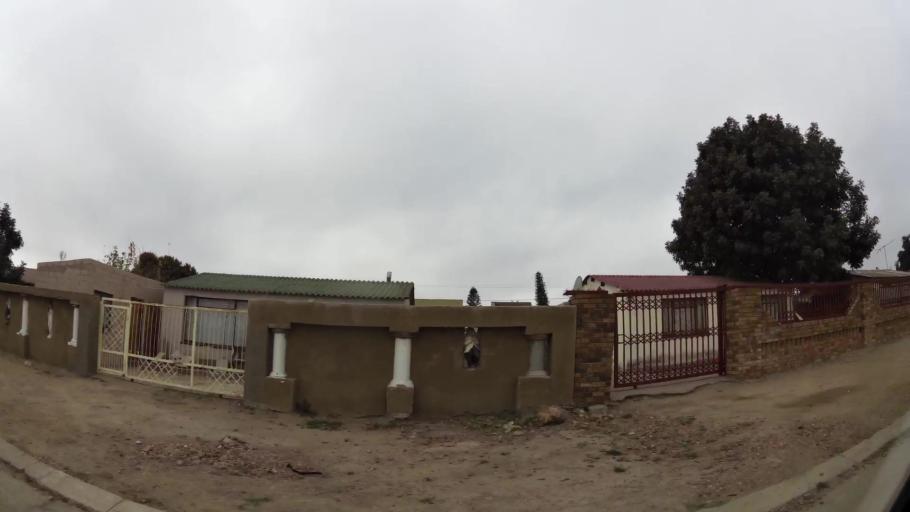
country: ZA
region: Limpopo
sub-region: Capricorn District Municipality
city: Polokwane
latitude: -23.8385
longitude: 29.3917
